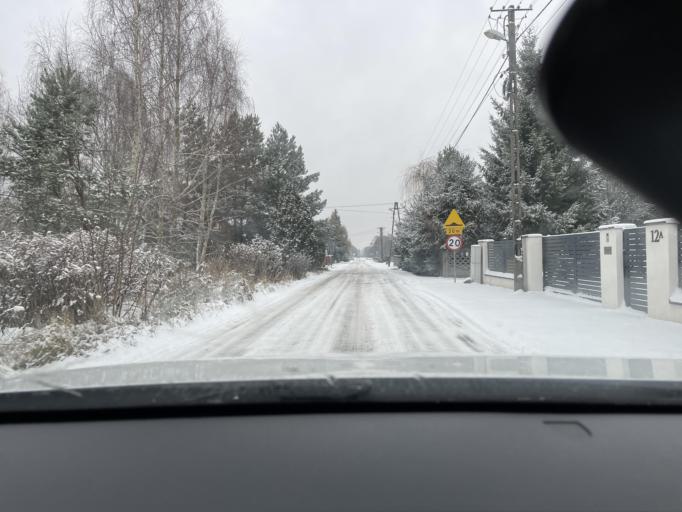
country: PL
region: Masovian Voivodeship
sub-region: Powiat zyrardowski
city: Zyrardow
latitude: 52.0313
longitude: 20.4581
